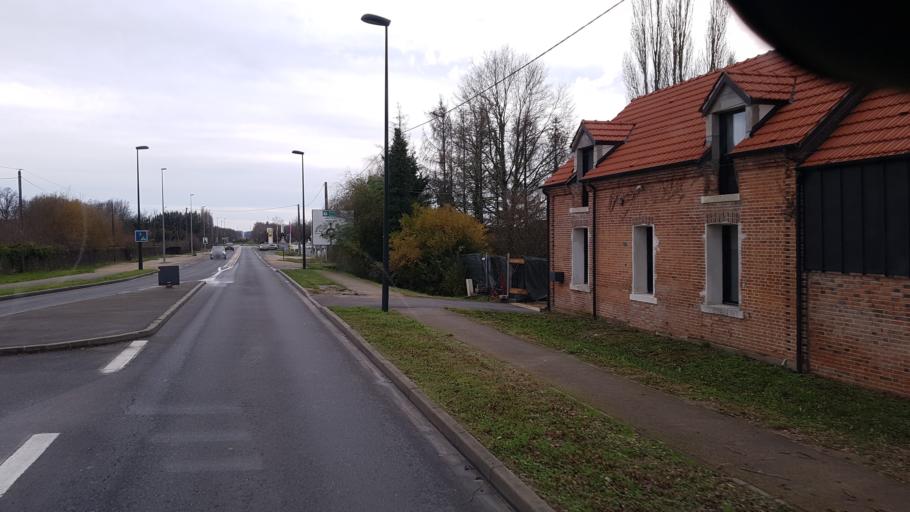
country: FR
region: Centre
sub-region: Departement du Loiret
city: La Ferte-Saint-Aubin
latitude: 47.7076
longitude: 1.9429
